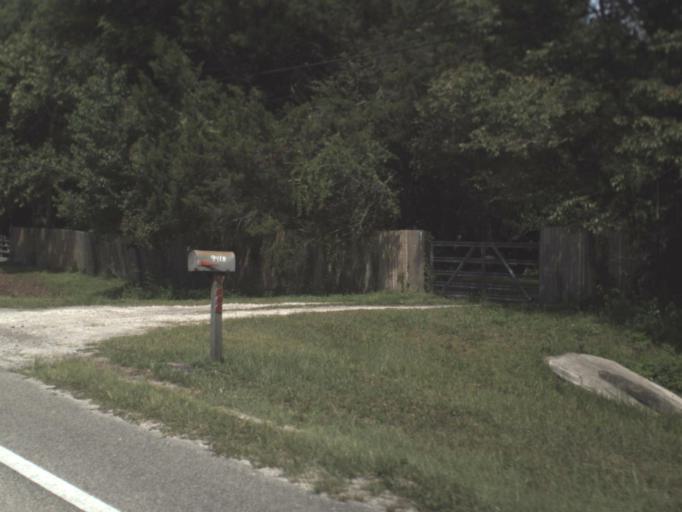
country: US
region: Florida
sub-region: Alachua County
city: Waldo
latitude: 29.7398
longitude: -82.2363
